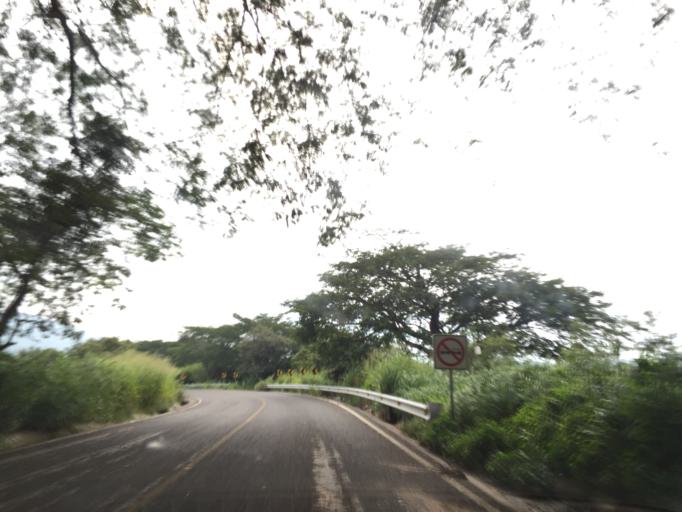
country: MX
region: Colima
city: Comala
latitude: 19.3419
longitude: -103.7810
